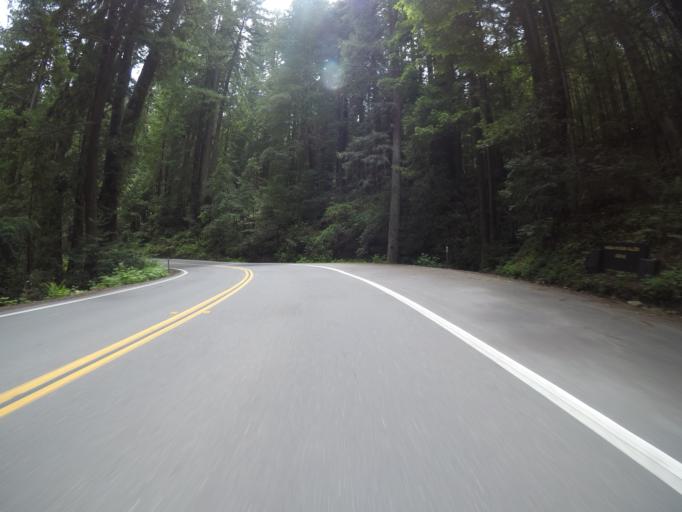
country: US
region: California
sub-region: Humboldt County
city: Rio Dell
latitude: 40.3727
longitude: -123.9252
